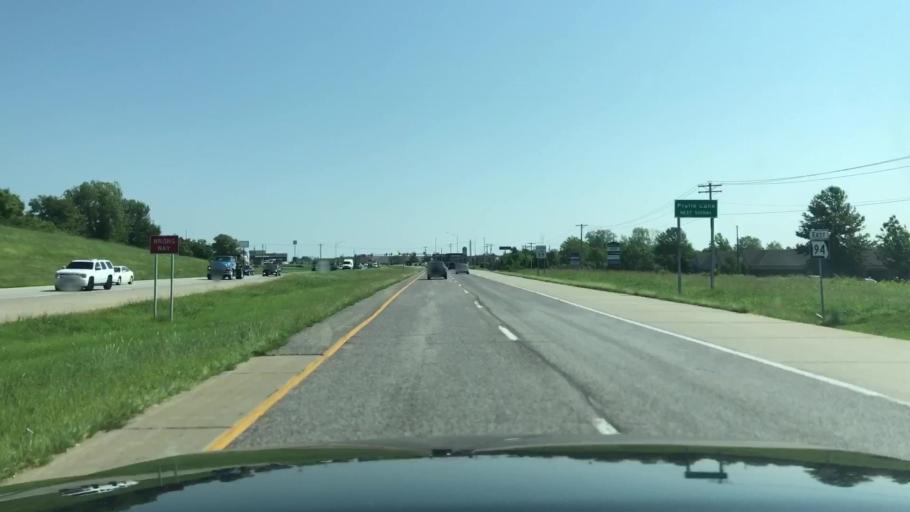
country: US
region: Missouri
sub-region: Saint Charles County
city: Saint Charles
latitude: 38.7594
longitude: -90.5346
